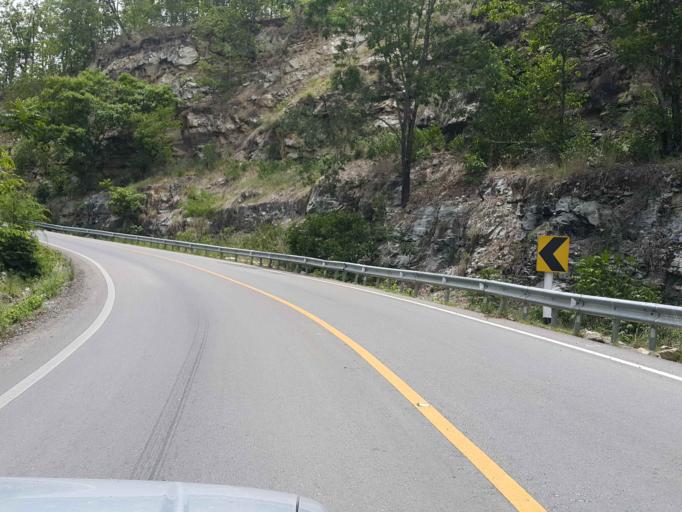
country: TH
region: Chiang Mai
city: Chom Thong
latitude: 18.5009
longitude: 98.6710
